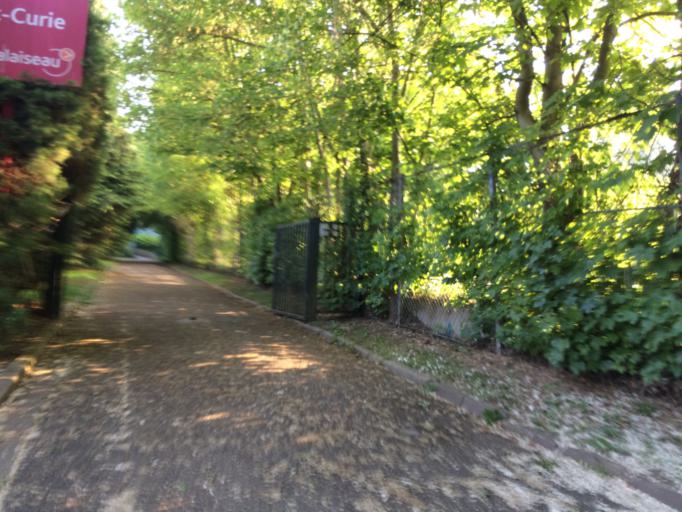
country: FR
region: Ile-de-France
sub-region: Departement de l'Essonne
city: Villebon-sur-Yvette
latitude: 48.7175
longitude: 2.2378
